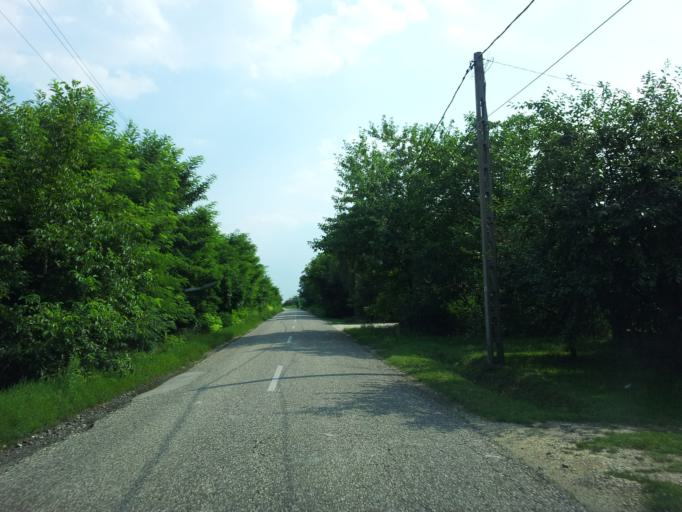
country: HU
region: Pest
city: Szigetujfalu
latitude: 47.2224
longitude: 18.9209
